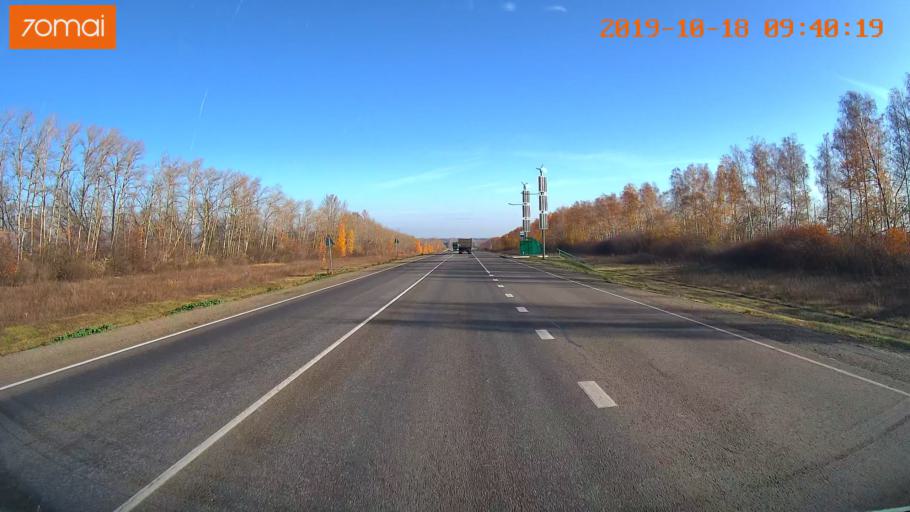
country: RU
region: Tula
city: Yefremov
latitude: 53.2627
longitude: 38.1465
